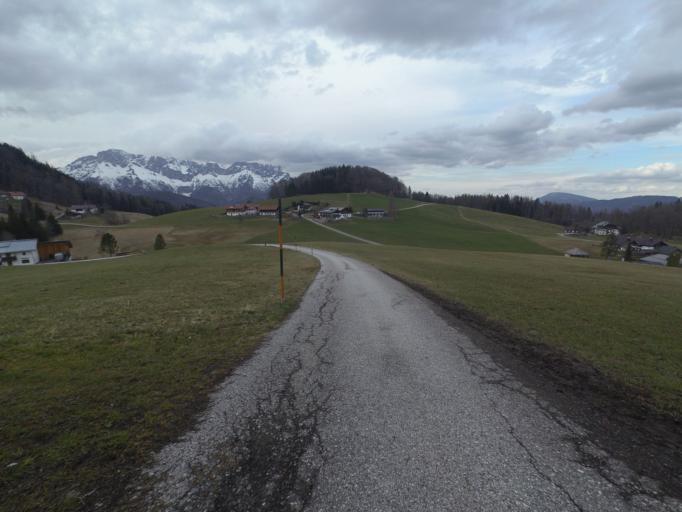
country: AT
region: Salzburg
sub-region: Politischer Bezirk Hallein
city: Hallein
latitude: 47.6634
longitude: 13.0785
